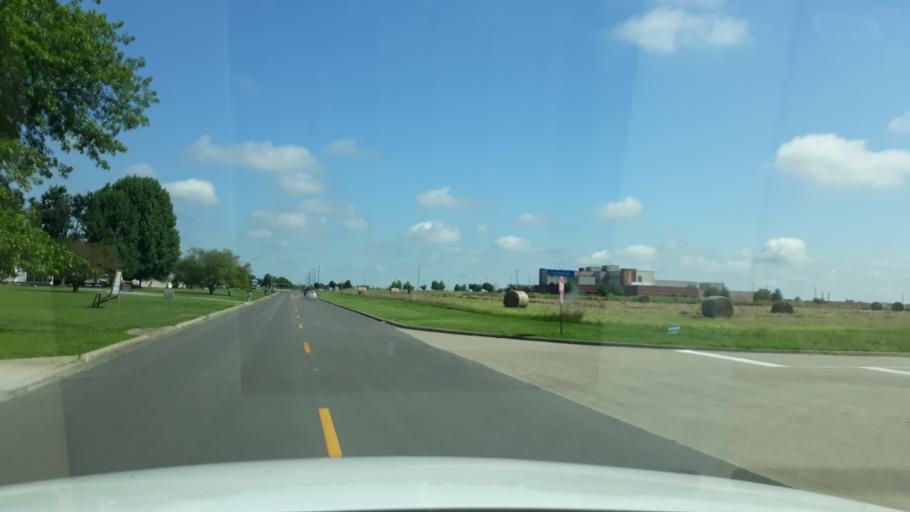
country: US
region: Illinois
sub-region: Williamson County
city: Energy
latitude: 37.7392
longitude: -88.9933
